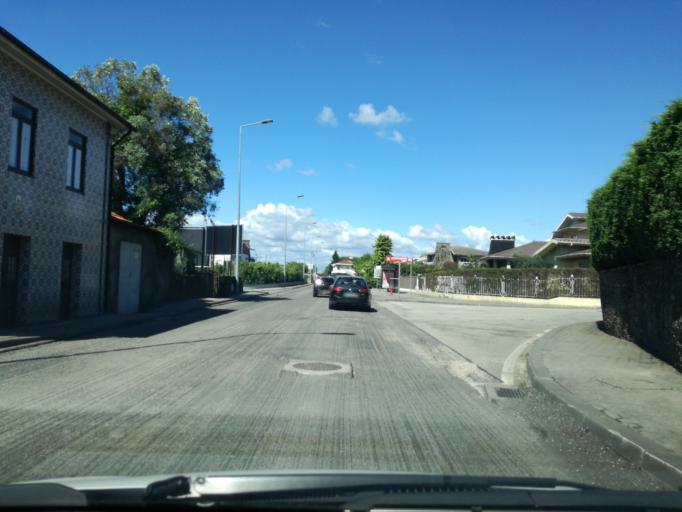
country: PT
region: Porto
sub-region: Trofa
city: Bougado
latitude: 41.3235
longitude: -8.5706
